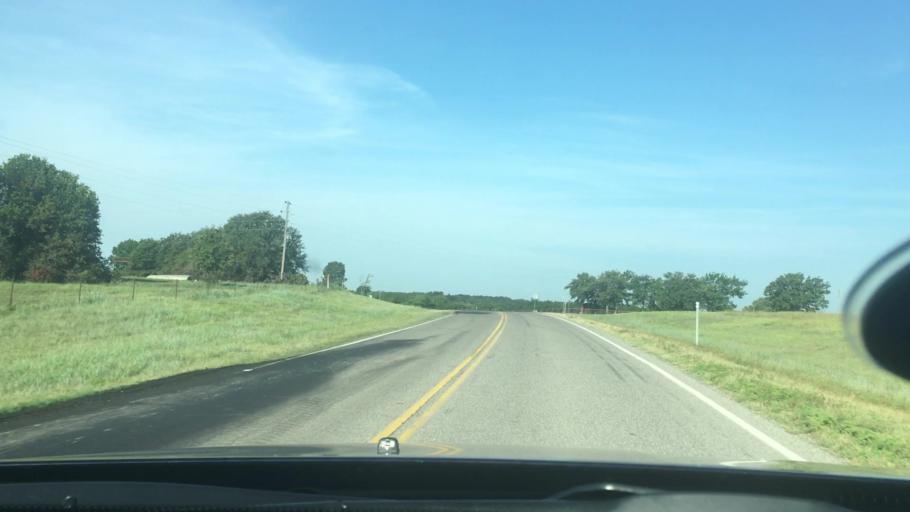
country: US
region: Oklahoma
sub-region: Garvin County
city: Pauls Valley
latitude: 34.6519
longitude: -97.3505
